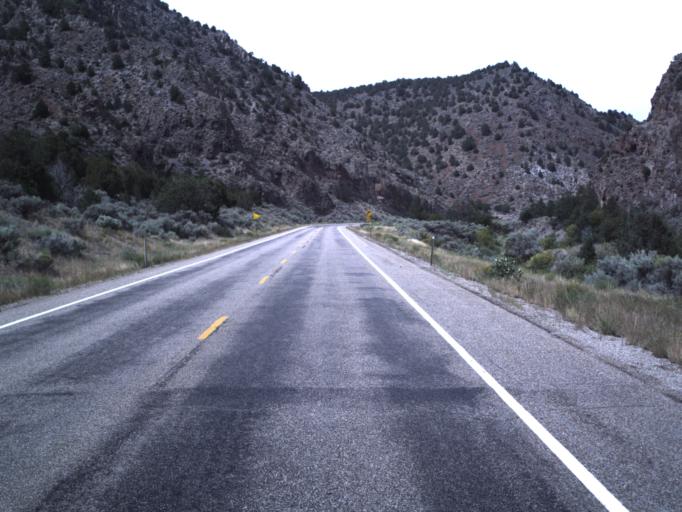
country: US
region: Utah
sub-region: Piute County
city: Junction
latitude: 38.1141
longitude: -112.3380
